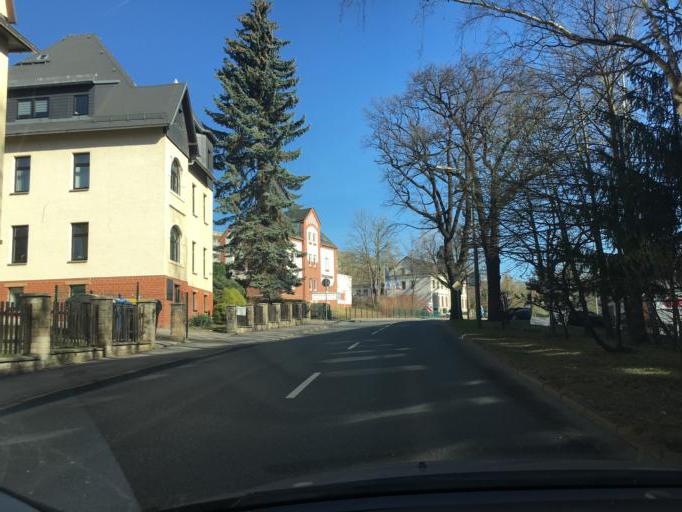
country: DE
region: Saxony
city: Neukirchen
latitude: 50.8059
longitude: 12.8975
